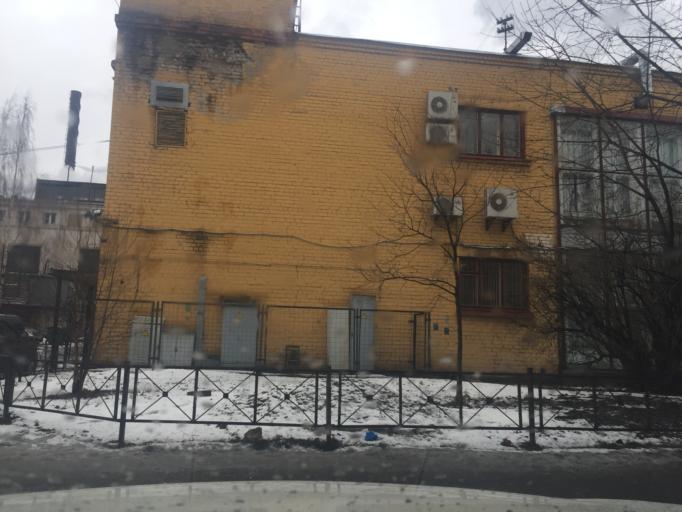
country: RU
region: Leningrad
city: Kalininskiy
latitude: 59.9557
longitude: 30.4215
